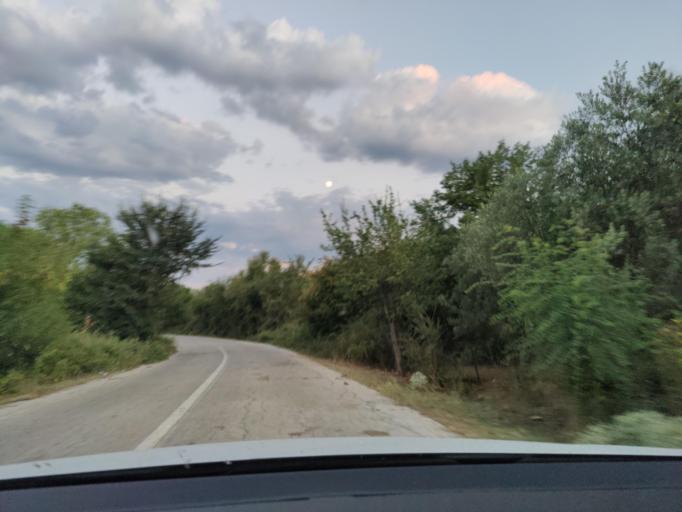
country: GR
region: Central Macedonia
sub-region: Nomos Serron
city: Chrysochorafa
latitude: 41.1598
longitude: 23.1899
